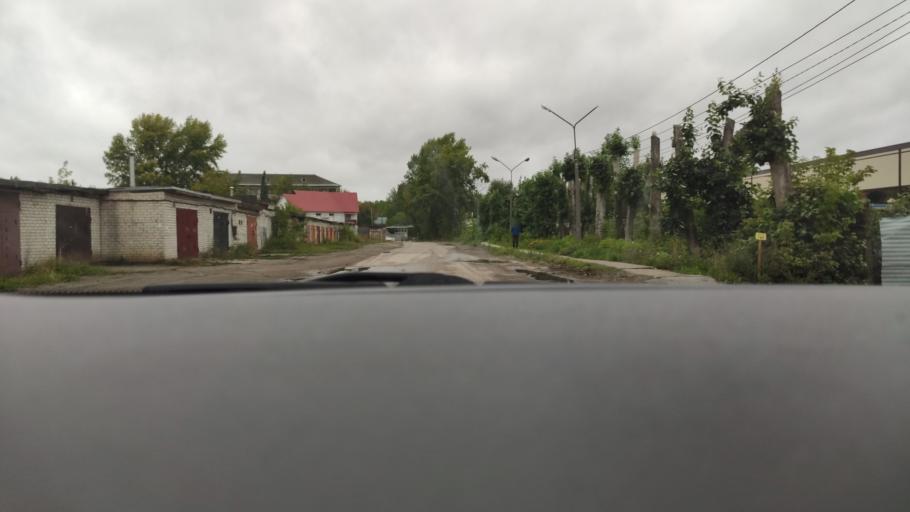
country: RU
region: Perm
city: Krasnokamsk
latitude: 58.0791
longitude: 55.7642
